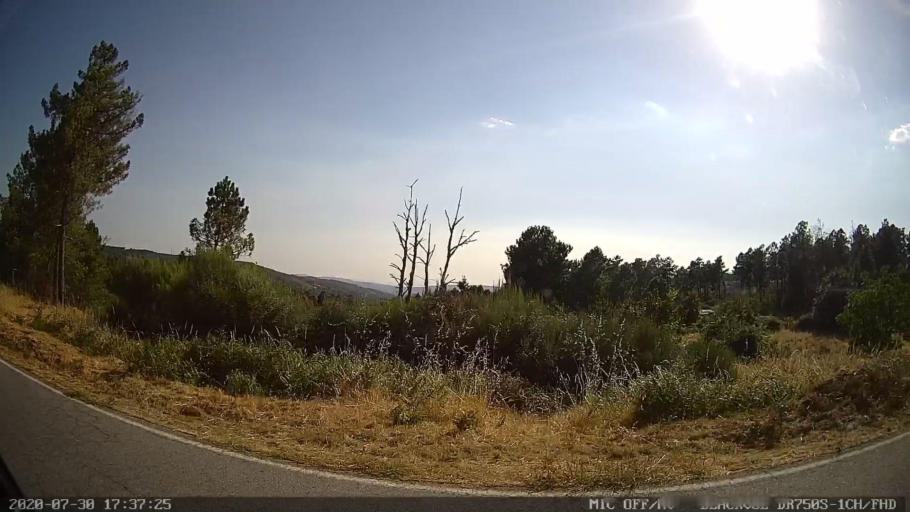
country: PT
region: Vila Real
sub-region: Murca
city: Murca
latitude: 41.3665
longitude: -7.4931
